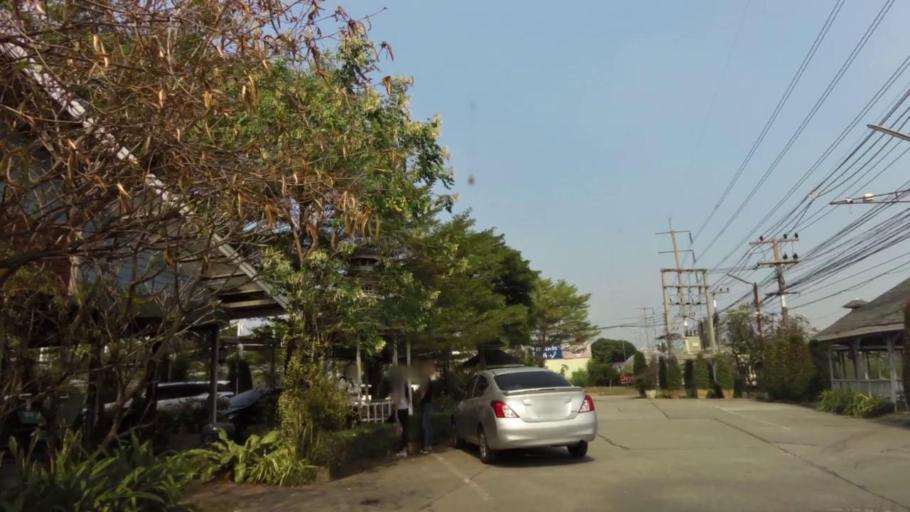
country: TH
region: Phra Nakhon Si Ayutthaya
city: Phra Nakhon Si Ayutthaya
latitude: 14.2936
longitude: 100.6124
